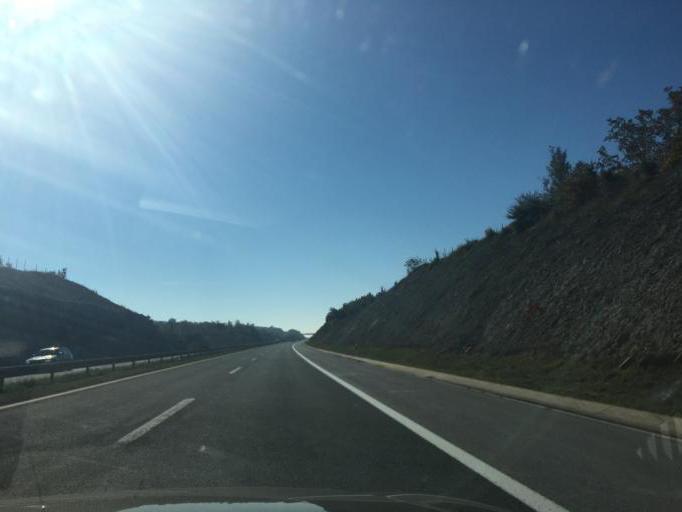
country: HR
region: Licko-Senjska
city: Gospic
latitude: 44.6916
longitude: 15.4030
